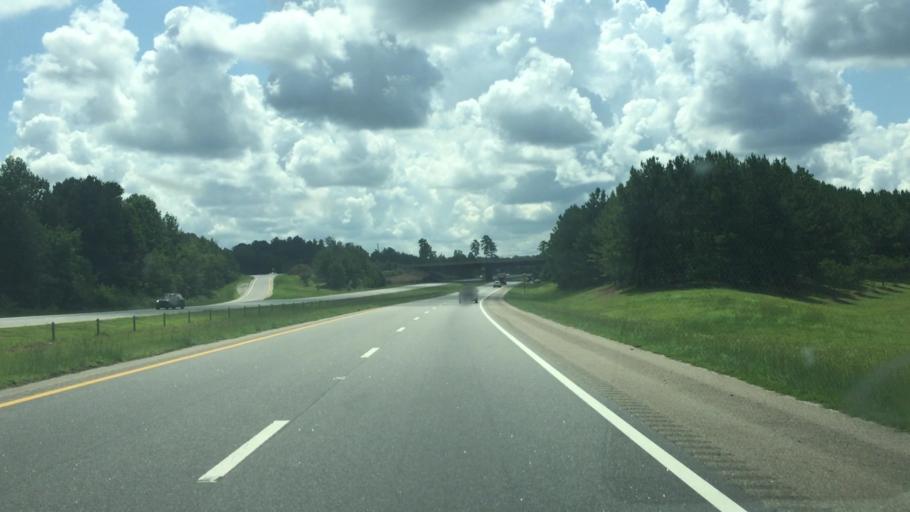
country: US
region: North Carolina
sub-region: Richmond County
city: Cordova
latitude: 34.9134
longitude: -79.7948
